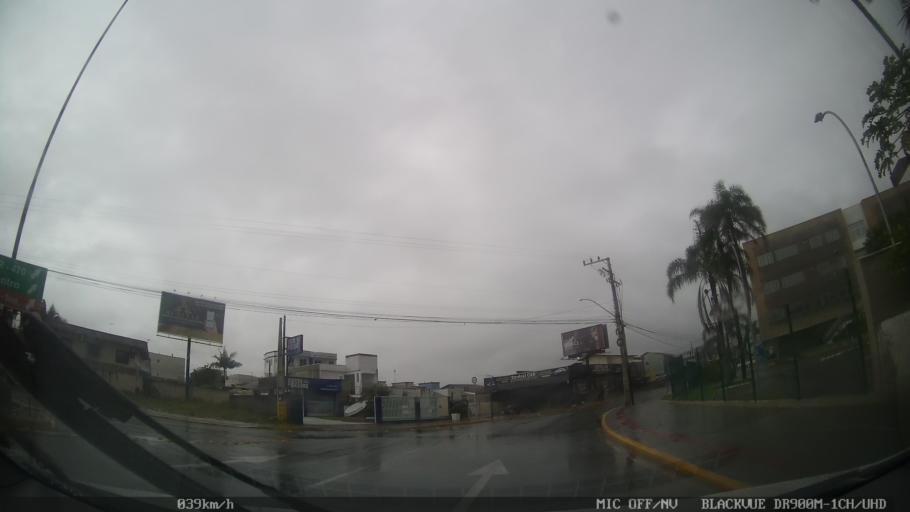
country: BR
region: Santa Catarina
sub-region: Navegantes
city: Navegantes
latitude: -26.8858
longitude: -48.6542
